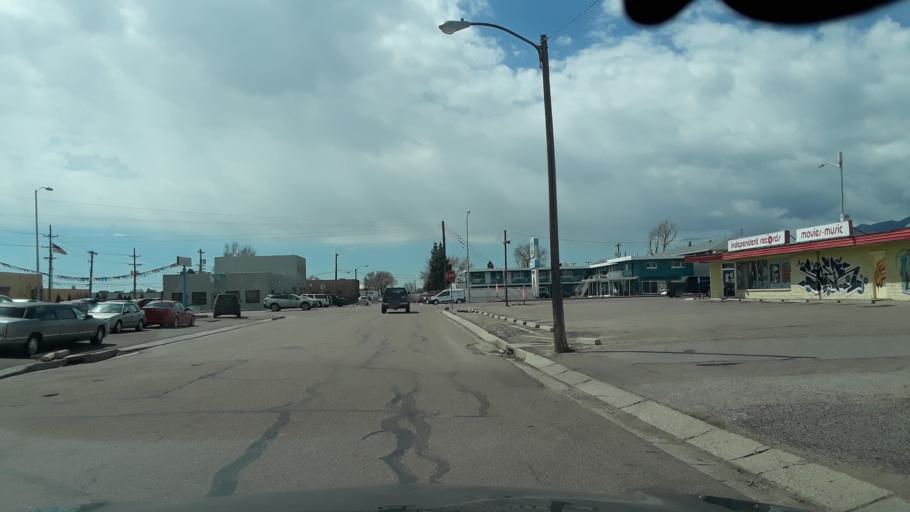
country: US
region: Colorado
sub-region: El Paso County
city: Colorado Springs
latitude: 38.8405
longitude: -104.7720
